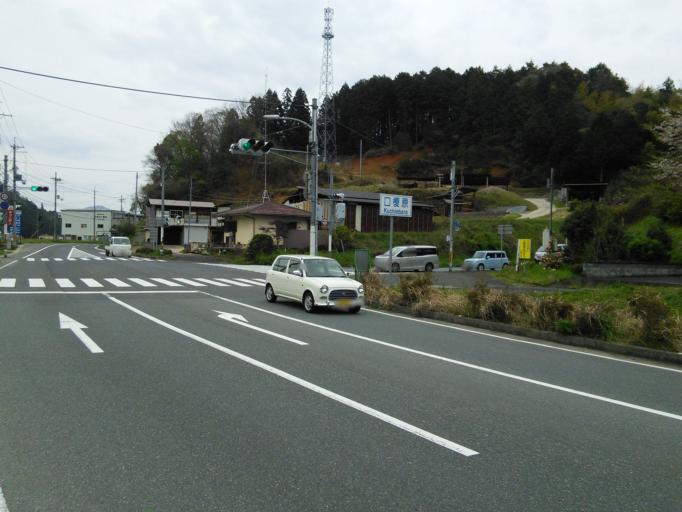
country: JP
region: Kyoto
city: Fukuchiyama
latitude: 35.2885
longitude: 135.0690
